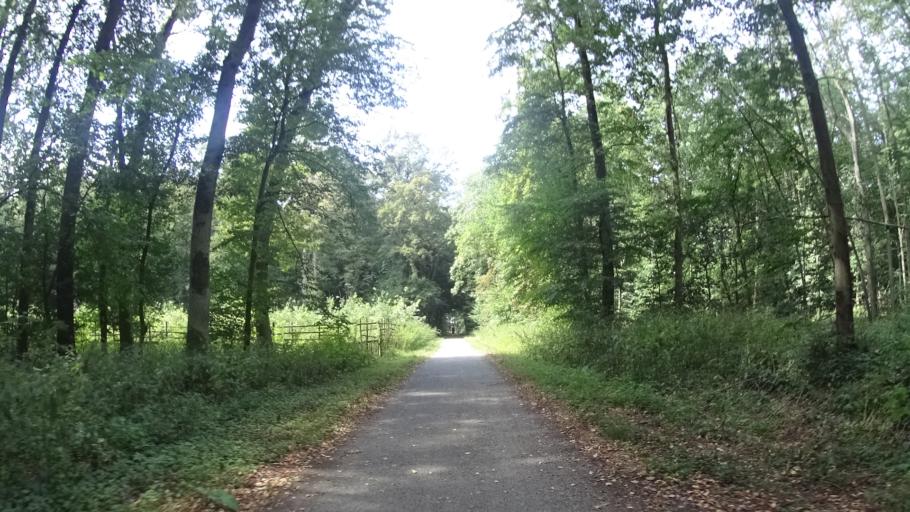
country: CZ
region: Olomoucky
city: Skrben
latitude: 49.6625
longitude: 17.1836
